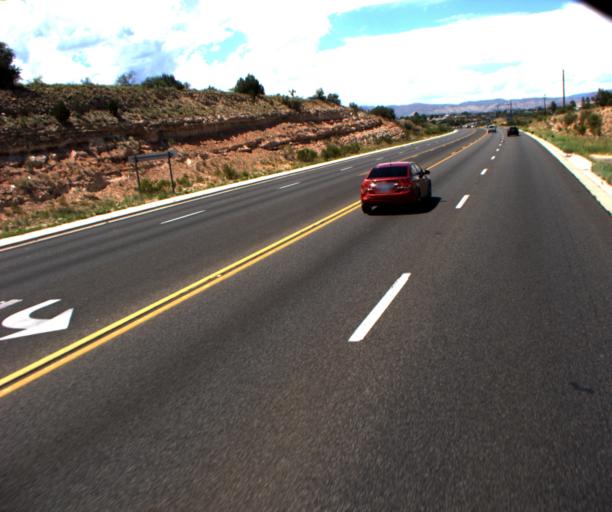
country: US
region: Arizona
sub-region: Yavapai County
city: Verde Village
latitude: 34.7050
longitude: -111.9909
